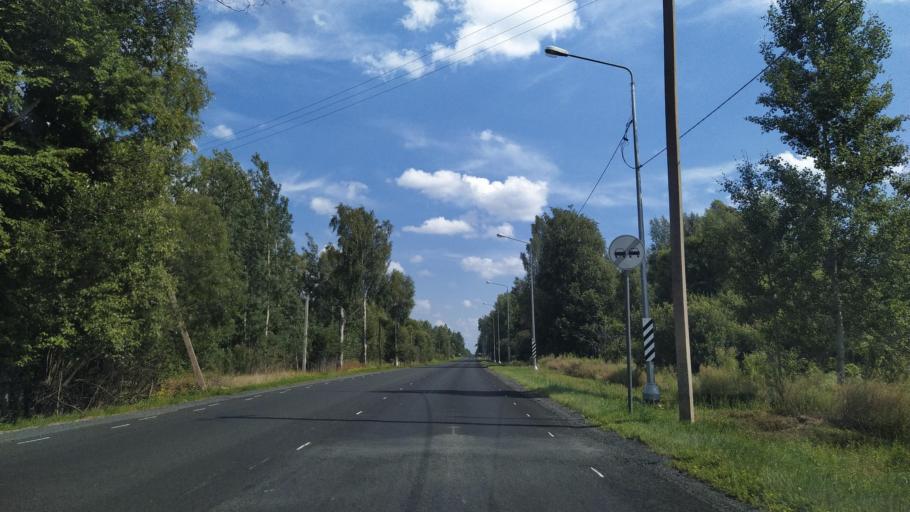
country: RU
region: Pskov
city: Porkhov
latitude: 57.7267
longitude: 29.1674
